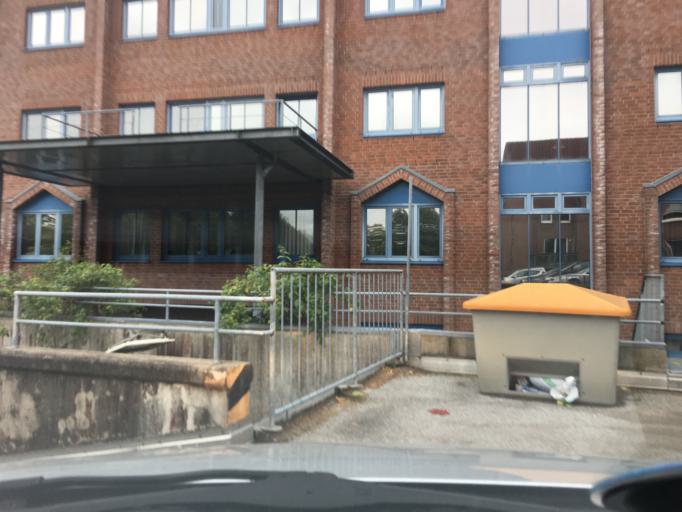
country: DE
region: Schleswig-Holstein
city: Kronshagen
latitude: 54.3375
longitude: 10.0976
